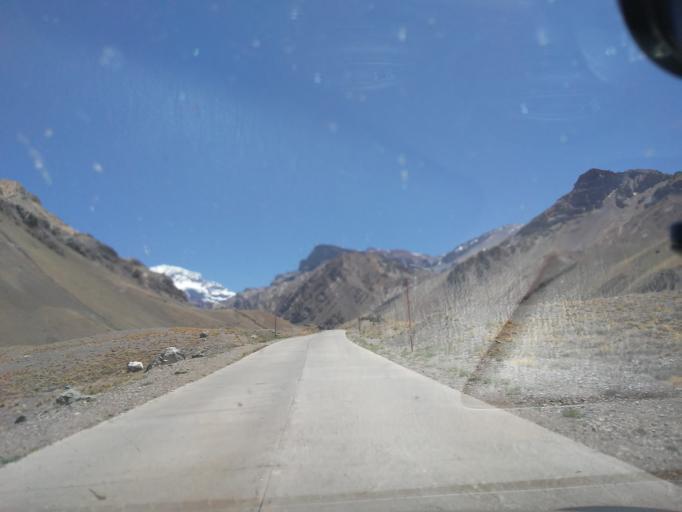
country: CL
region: Valparaiso
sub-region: Provincia de Los Andes
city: Los Andes
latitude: -32.8206
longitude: -69.9421
